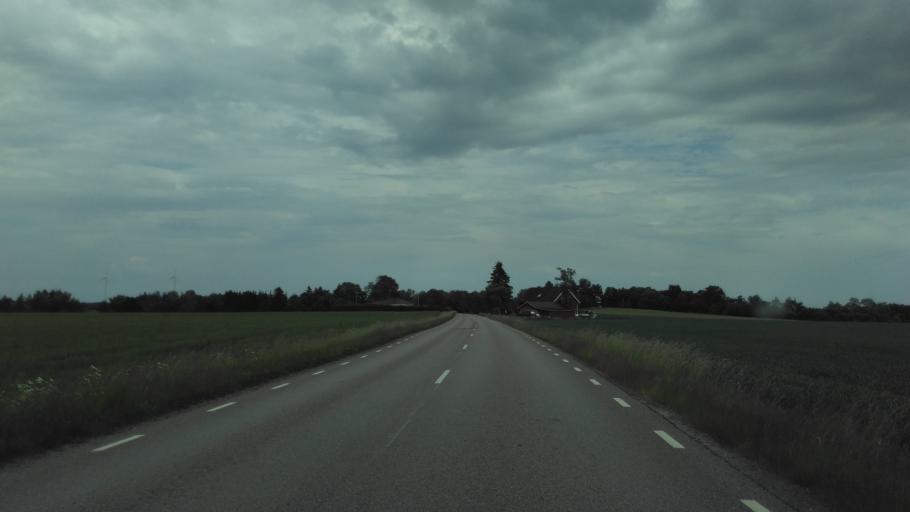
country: SE
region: Vaestra Goetaland
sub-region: Vara Kommun
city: Kvanum
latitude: 58.3960
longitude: 13.1571
